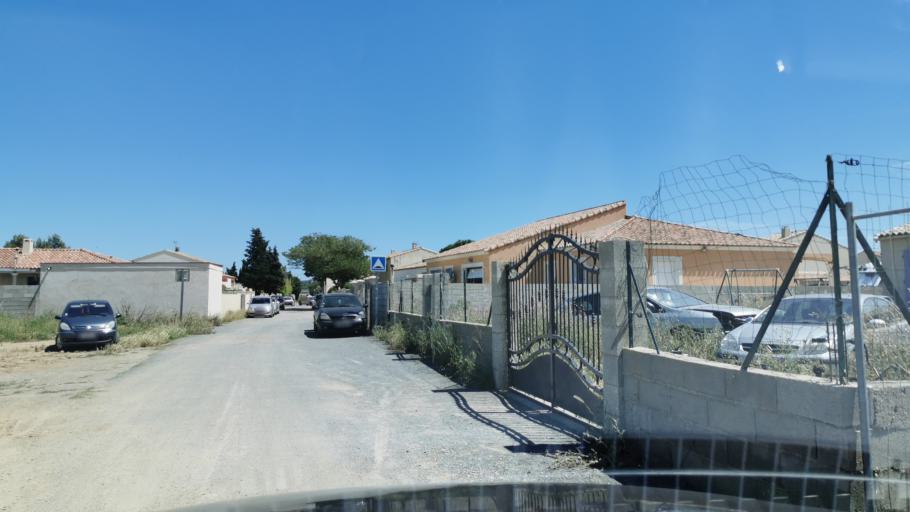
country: FR
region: Languedoc-Roussillon
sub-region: Departement de l'Aude
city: Canet
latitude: 43.2170
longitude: 2.8525
